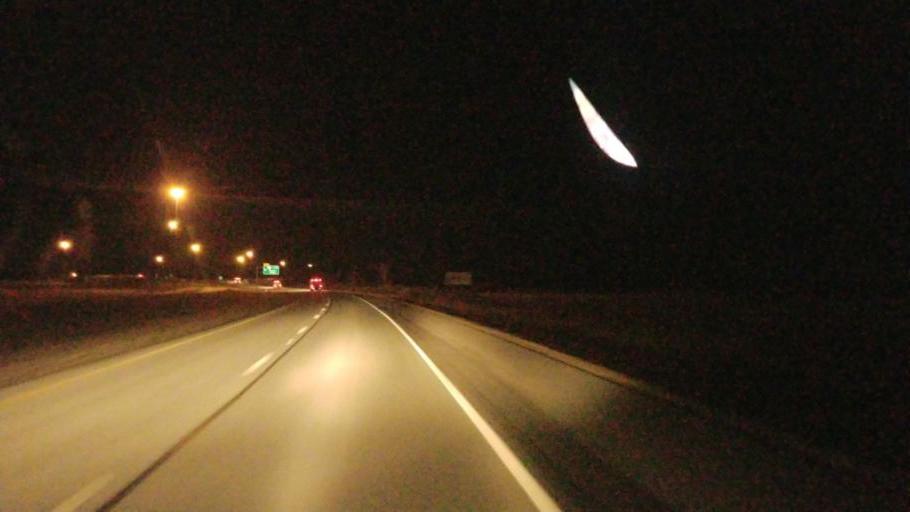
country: US
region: Ohio
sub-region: Allen County
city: Bluffton
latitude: 40.8253
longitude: -83.9640
